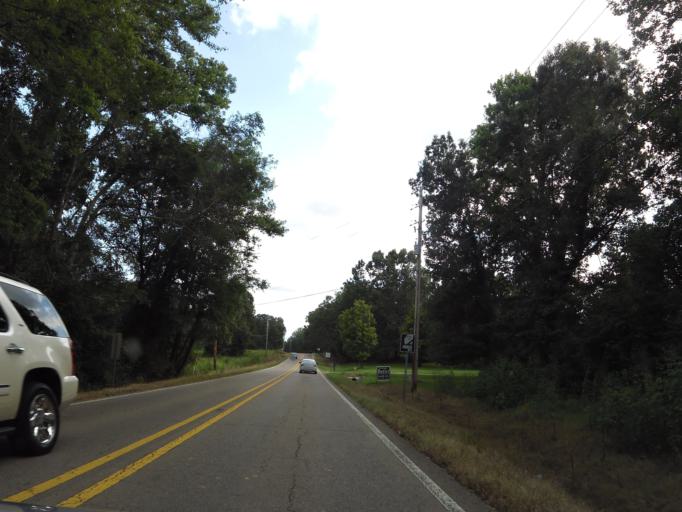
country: US
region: Mississippi
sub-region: Alcorn County
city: Farmington
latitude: 34.9950
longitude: -88.4630
